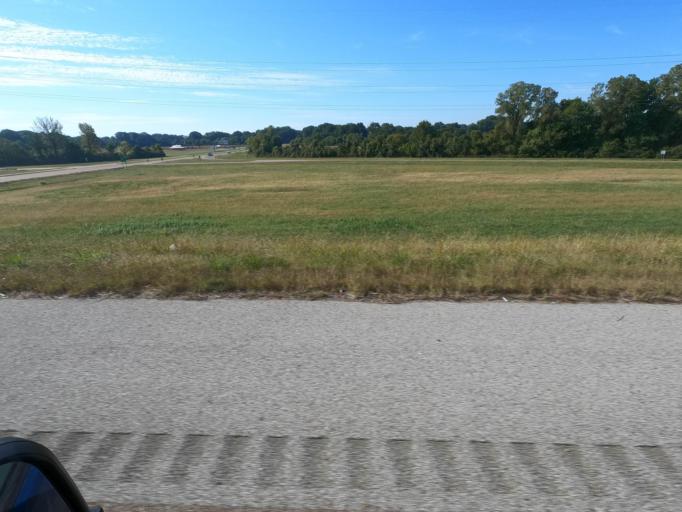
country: US
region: Tennessee
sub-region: Shelby County
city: Millington
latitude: 35.3196
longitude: -89.8744
